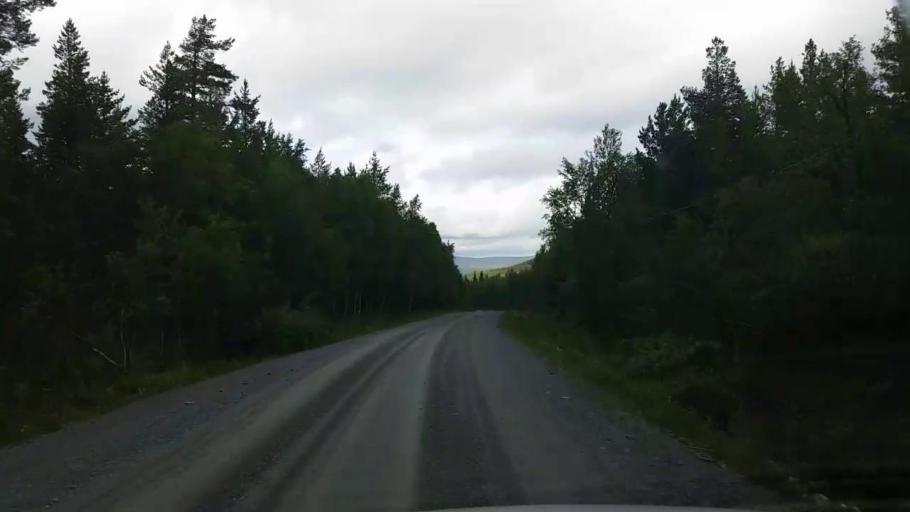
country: NO
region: Hedmark
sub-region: Engerdal
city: Engerdal
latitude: 62.4074
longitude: 12.6688
